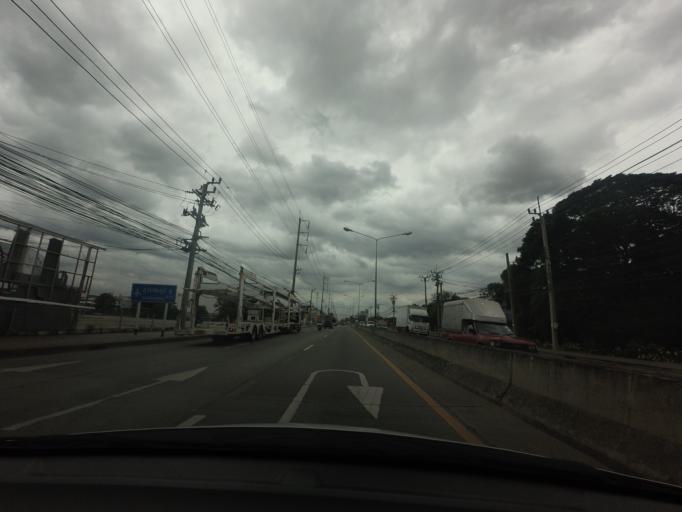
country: TH
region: Bangkok
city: Min Buri
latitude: 13.7727
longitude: 100.7463
